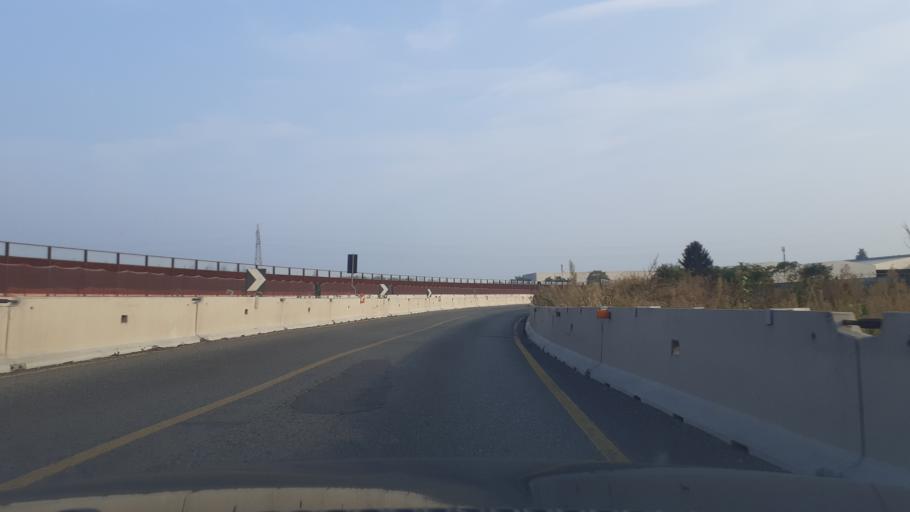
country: IT
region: Lombardy
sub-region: Citta metropolitana di Milano
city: Cormano
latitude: 45.5544
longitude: 9.1456
